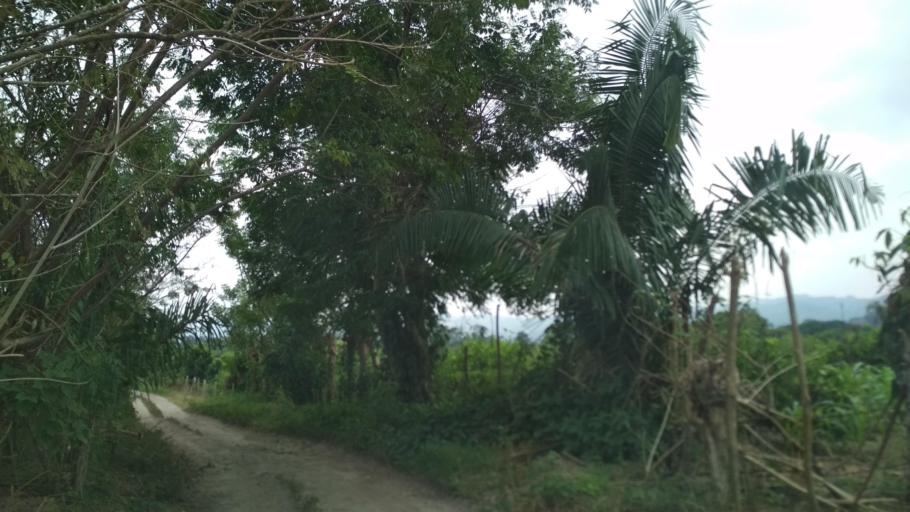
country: MM
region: Kayah
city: Loikaw
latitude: 20.2139
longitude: 97.3321
